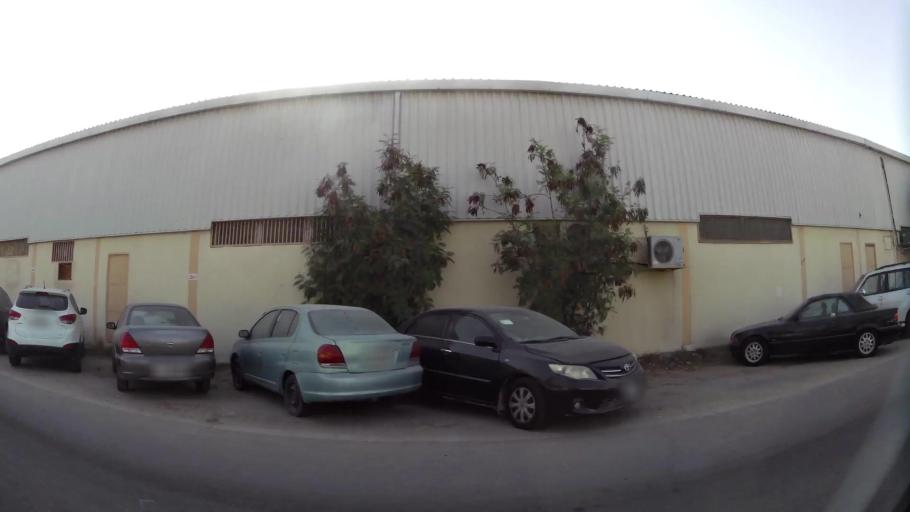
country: AE
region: Ash Shariqah
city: Sharjah
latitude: 25.2329
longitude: 55.3737
